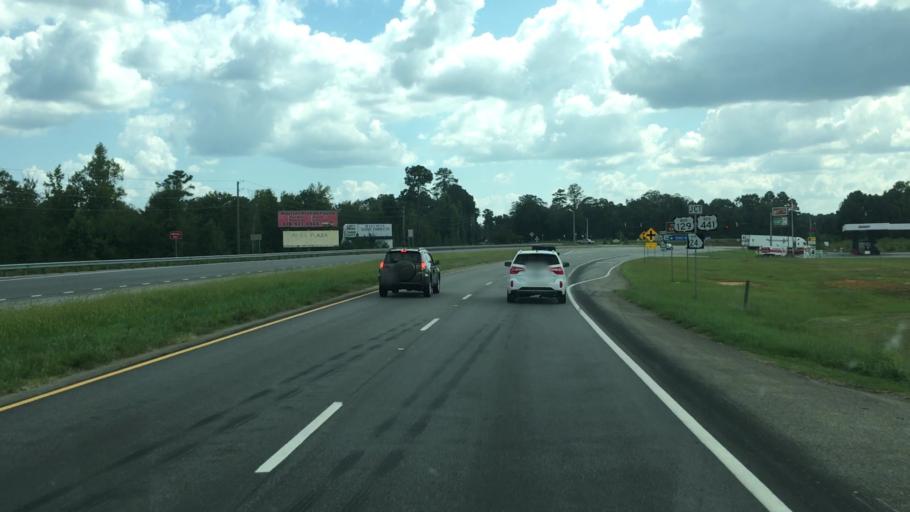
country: US
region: Georgia
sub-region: Putnam County
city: Eatonton
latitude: 33.3493
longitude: -83.3917
